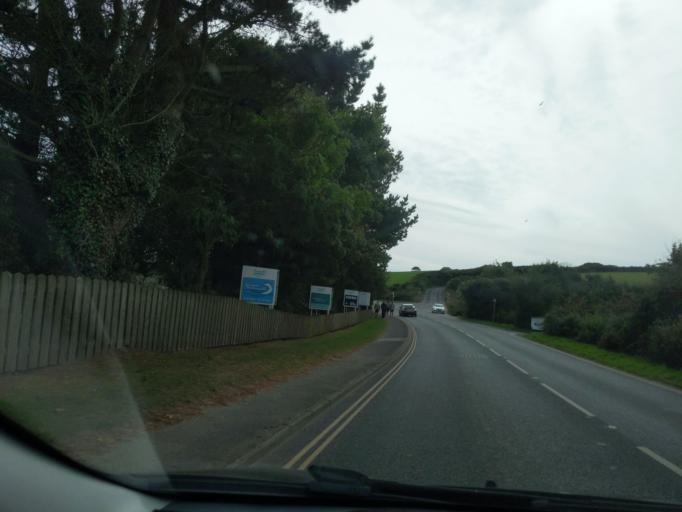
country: GB
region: England
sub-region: Cornwall
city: Mevagissey
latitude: 50.2898
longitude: -4.7865
